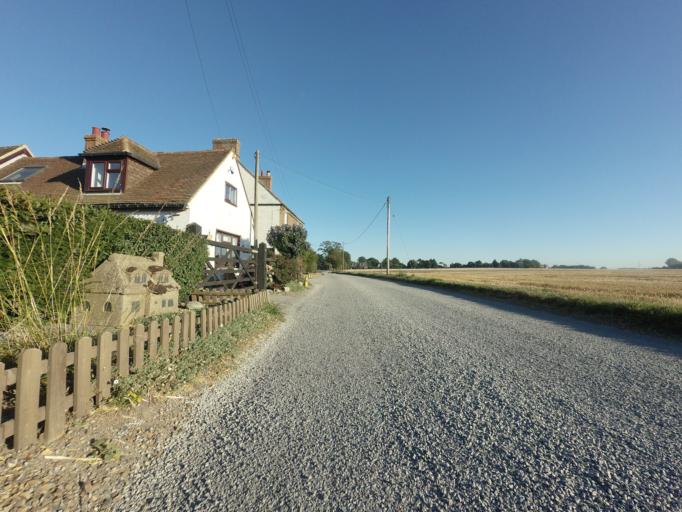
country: GB
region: England
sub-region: Kent
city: Herne Bay
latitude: 51.3369
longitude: 1.1904
